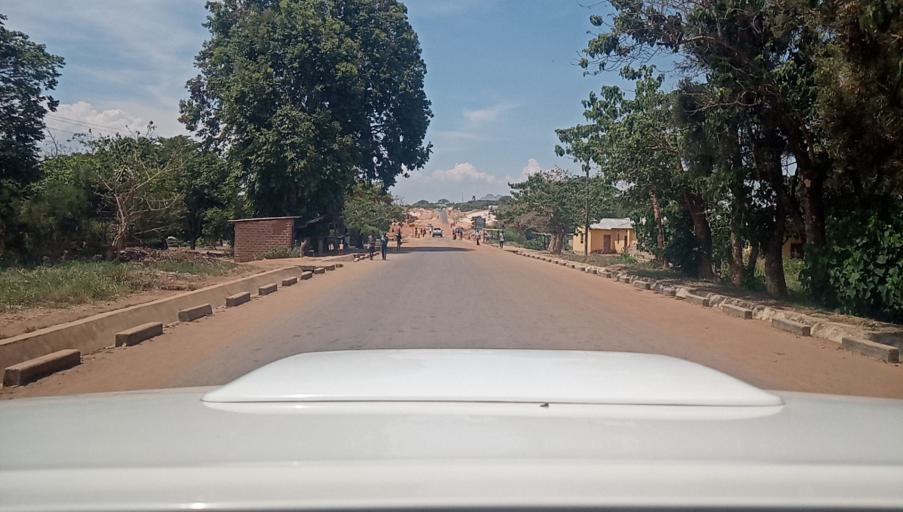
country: ZM
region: Luapula
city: Samfya
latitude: -11.3553
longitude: 29.5582
